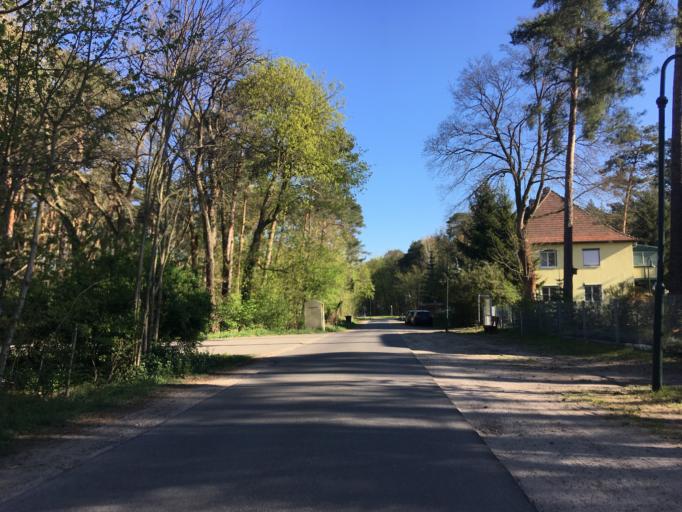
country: DE
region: Brandenburg
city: Bernau bei Berlin
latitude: 52.7003
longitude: 13.5440
